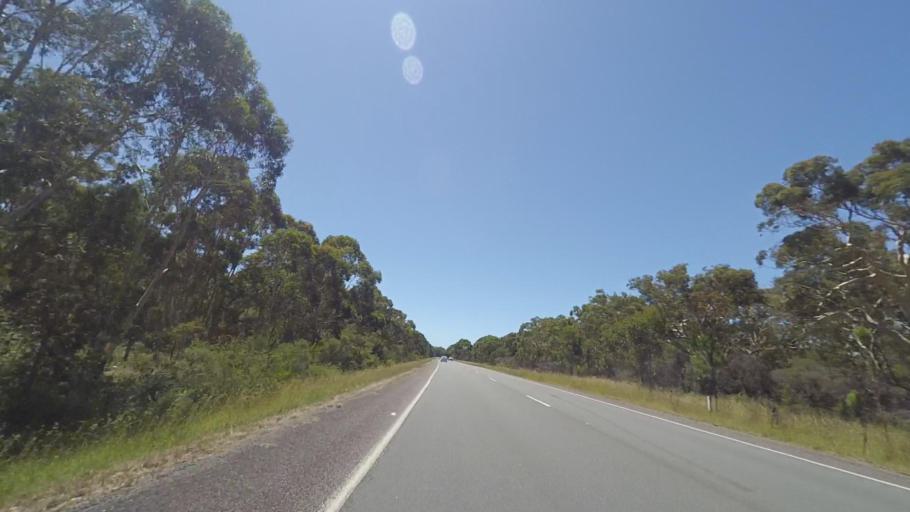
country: AU
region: New South Wales
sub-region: Port Stephens Shire
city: Medowie
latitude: -32.7833
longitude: 151.8909
